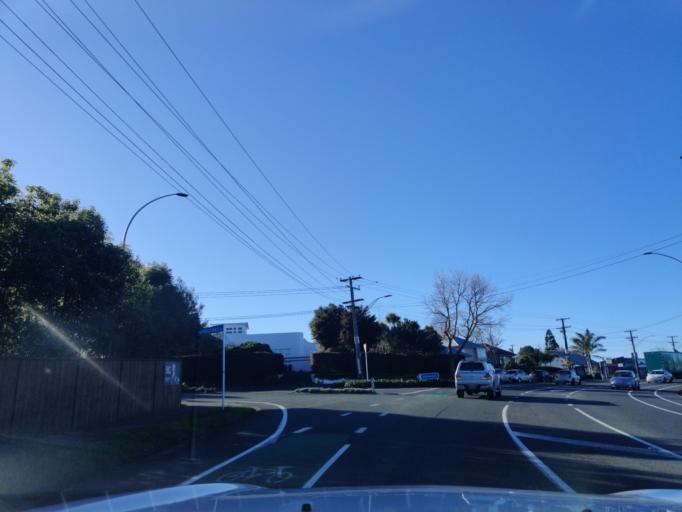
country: NZ
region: Waikato
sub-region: Hamilton City
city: Hamilton
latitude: -37.7979
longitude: 175.3146
